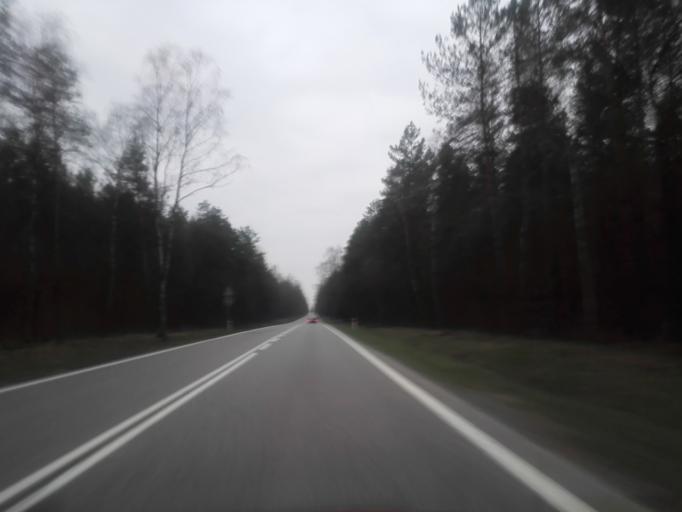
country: PL
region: Podlasie
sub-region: Powiat kolnenski
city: Stawiski
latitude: 53.3498
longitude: 22.1596
